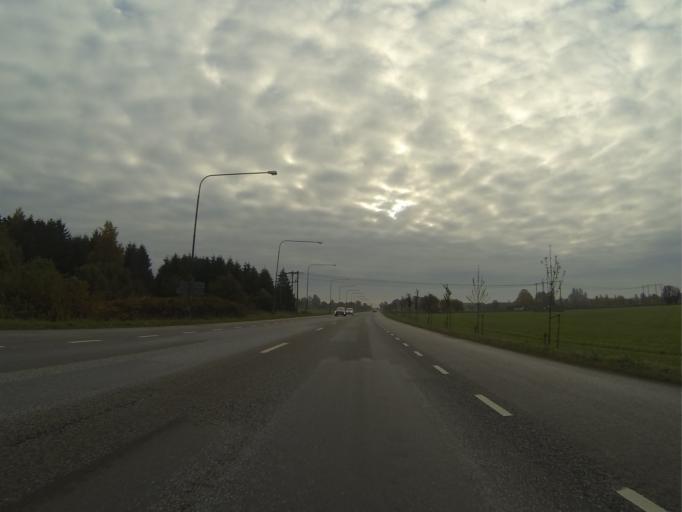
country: SE
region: Skane
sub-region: Tomelilla Kommun
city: Tomelilla
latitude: 55.5552
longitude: 13.9325
